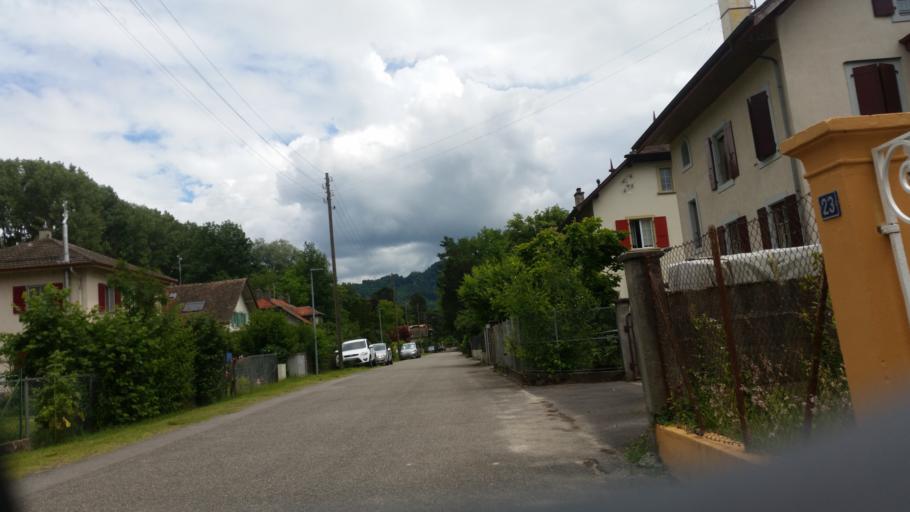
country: CH
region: Vaud
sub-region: Jura-Nord vaudois District
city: Yvonand
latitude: 46.8028
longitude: 6.7412
